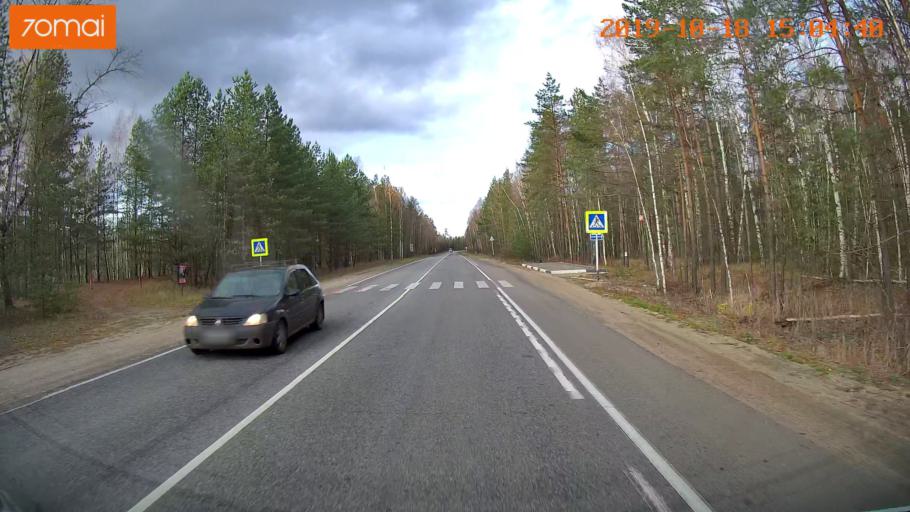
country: RU
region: Vladimir
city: Kurlovo
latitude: 55.5050
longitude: 40.5714
